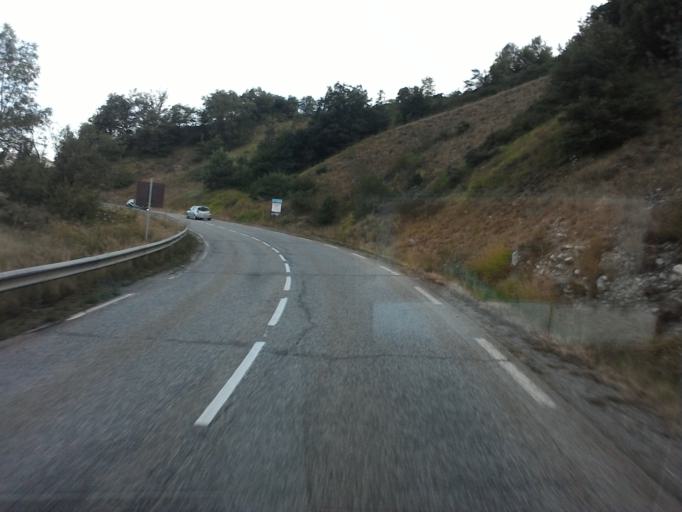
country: FR
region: Rhone-Alpes
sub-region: Departement de l'Isere
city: La Mure
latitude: 44.8696
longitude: 5.8420
